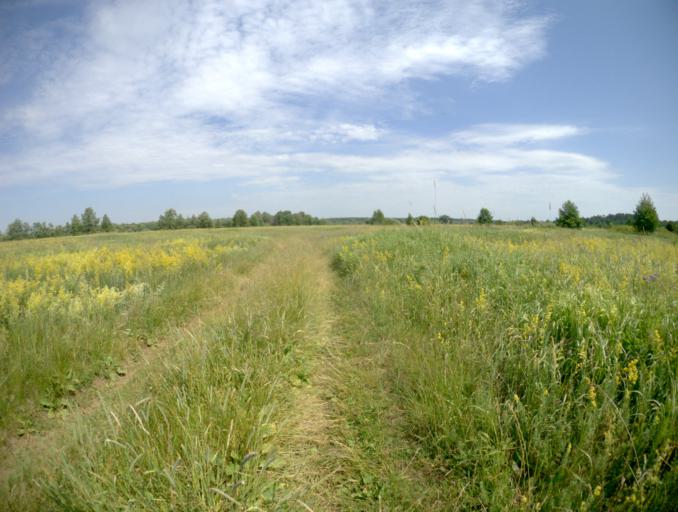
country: RU
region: Vladimir
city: Vorsha
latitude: 56.0321
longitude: 40.1822
